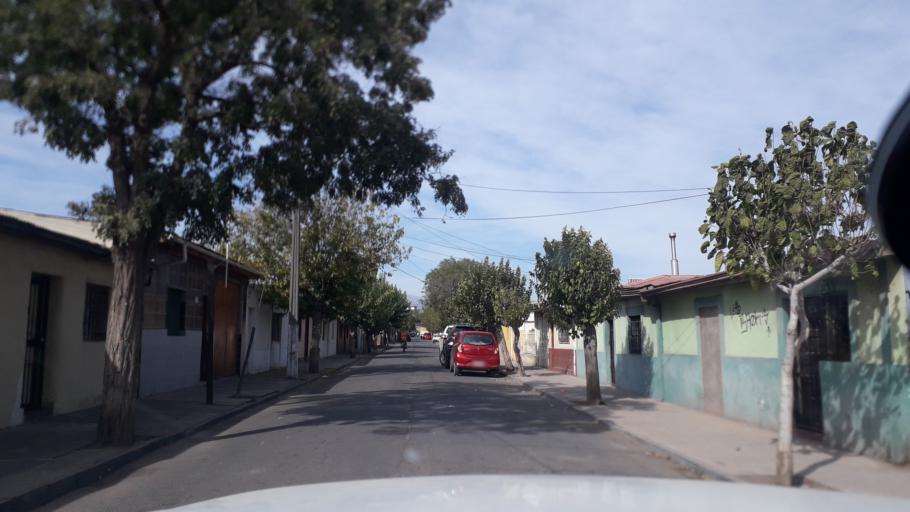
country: CL
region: Valparaiso
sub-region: Provincia de San Felipe
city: San Felipe
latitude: -32.7484
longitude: -70.7338
